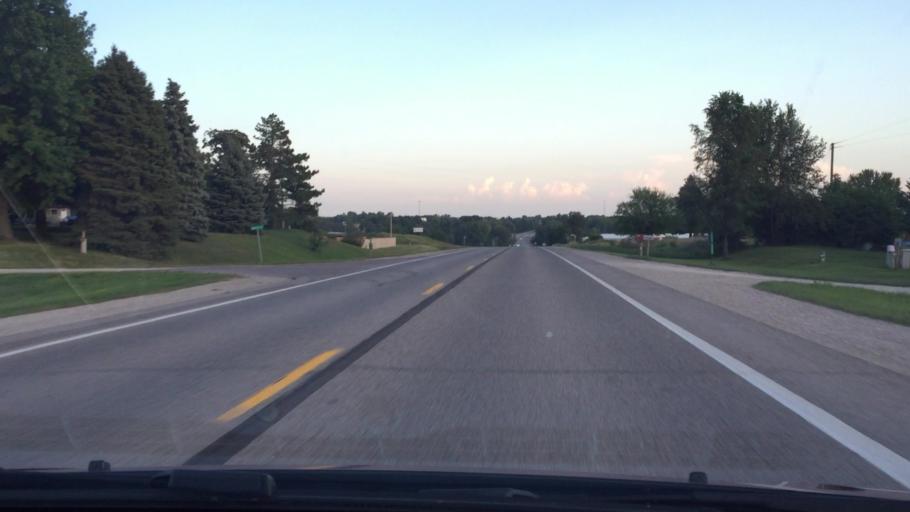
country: US
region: Iowa
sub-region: Muscatine County
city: Muscatine
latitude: 41.4682
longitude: -91.0356
